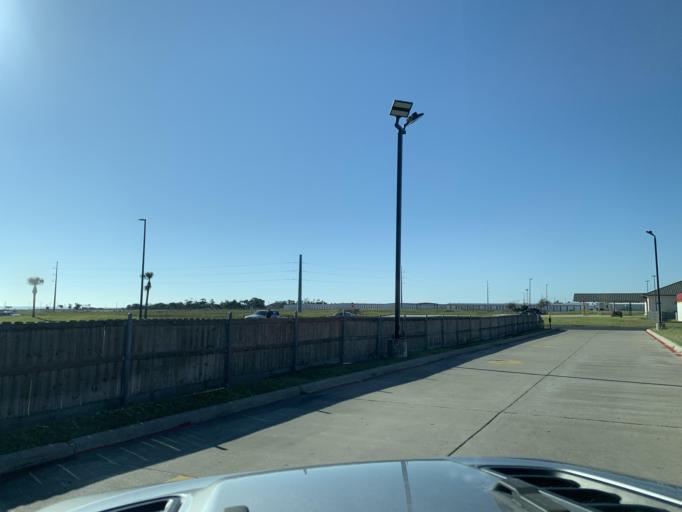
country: US
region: Texas
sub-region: Nueces County
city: Corpus Christi
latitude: 27.6657
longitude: -97.2832
